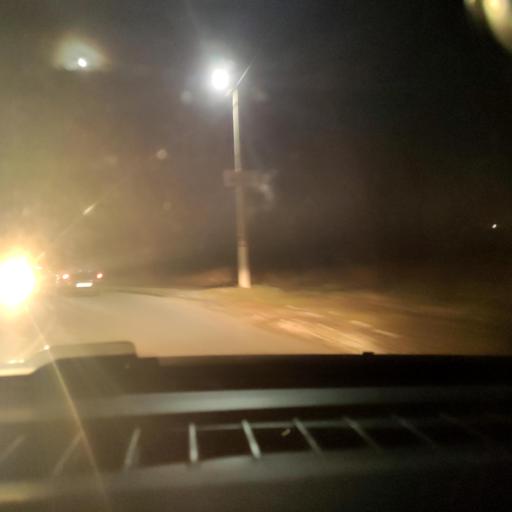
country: RU
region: Voronezj
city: Novaya Usman'
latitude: 51.6647
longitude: 39.3254
